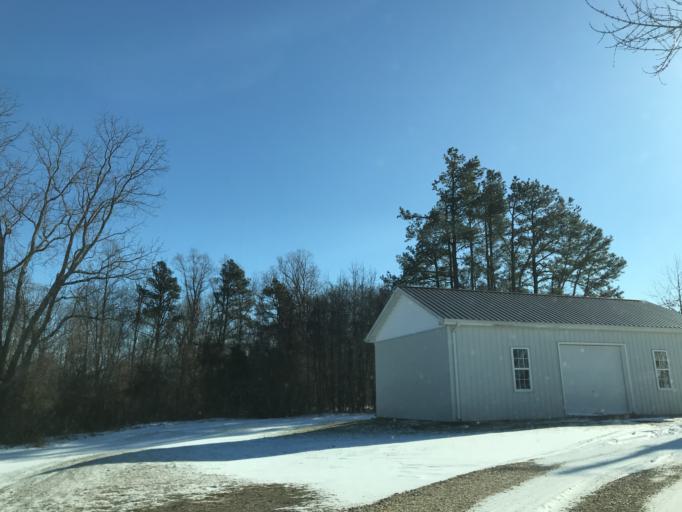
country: US
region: Maryland
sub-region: Charles County
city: La Plata
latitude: 38.4348
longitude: -76.9102
